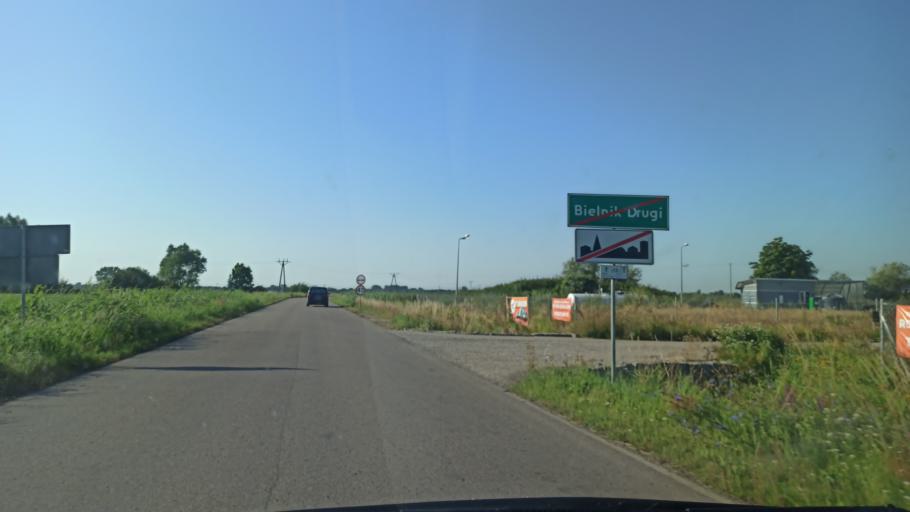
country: PL
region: Warmian-Masurian Voivodeship
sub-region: Powiat elblaski
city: Elblag
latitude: 54.1882
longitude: 19.3325
